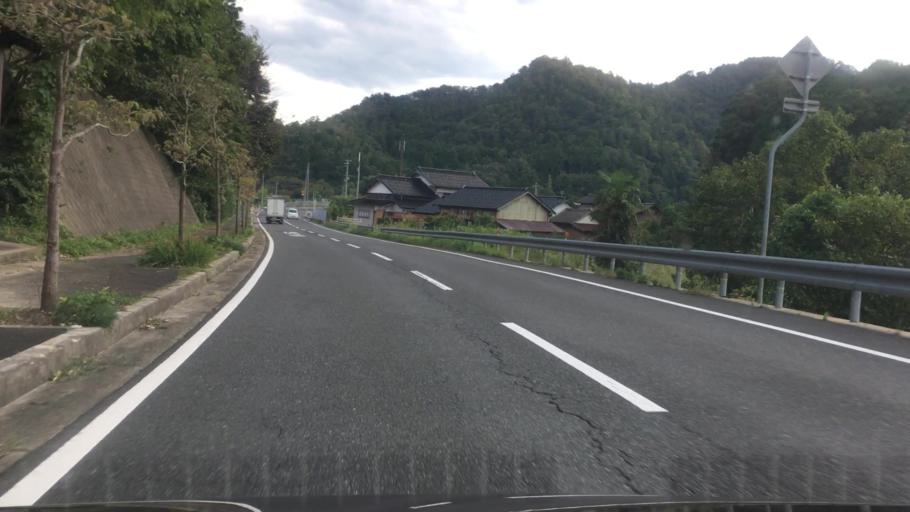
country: JP
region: Hyogo
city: Toyooka
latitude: 35.6115
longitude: 134.9190
